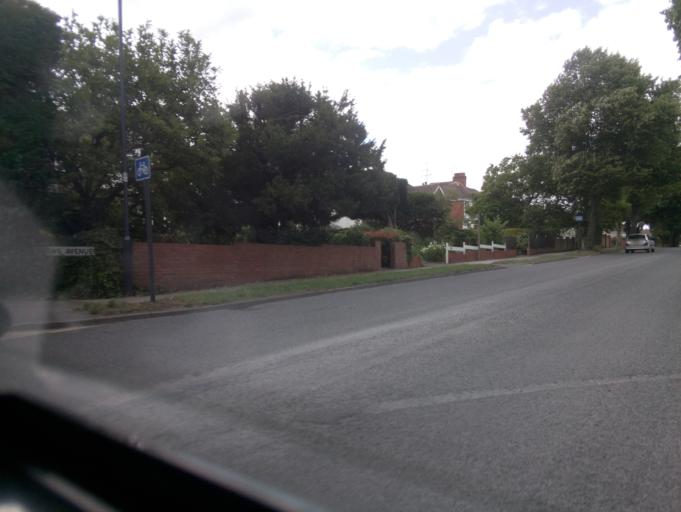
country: GB
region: England
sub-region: Warwickshire
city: Nuneaton
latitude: 52.5340
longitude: -1.4657
